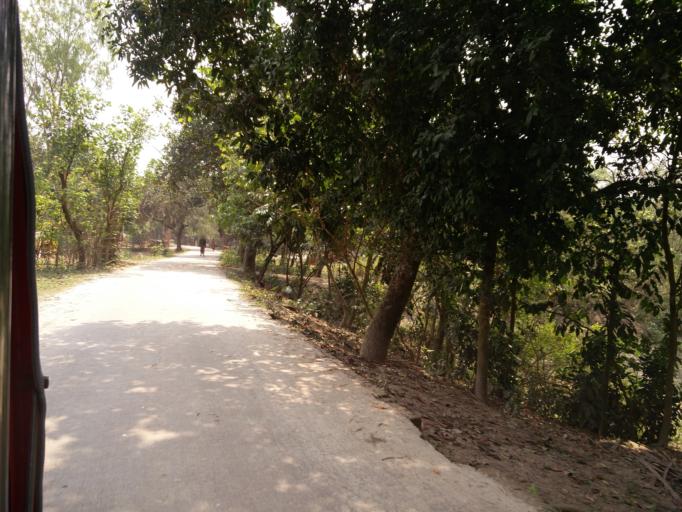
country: BD
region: Dhaka
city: Muktagacha
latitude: 24.8859
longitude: 90.2772
